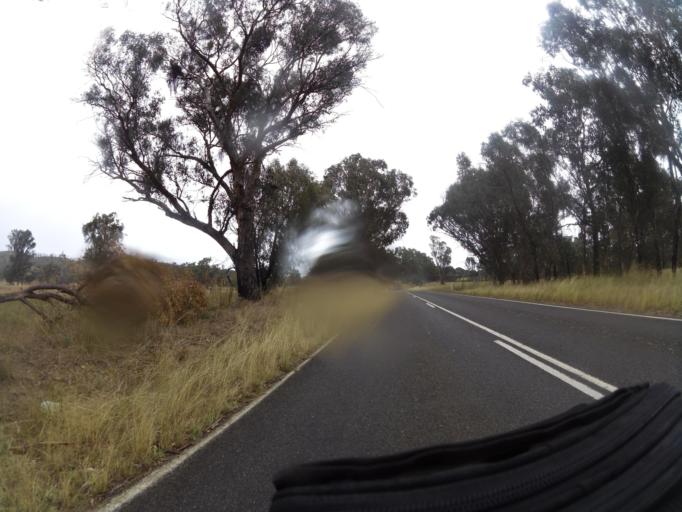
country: AU
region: New South Wales
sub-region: Greater Hume Shire
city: Holbrook
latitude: -36.2081
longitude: 147.8098
